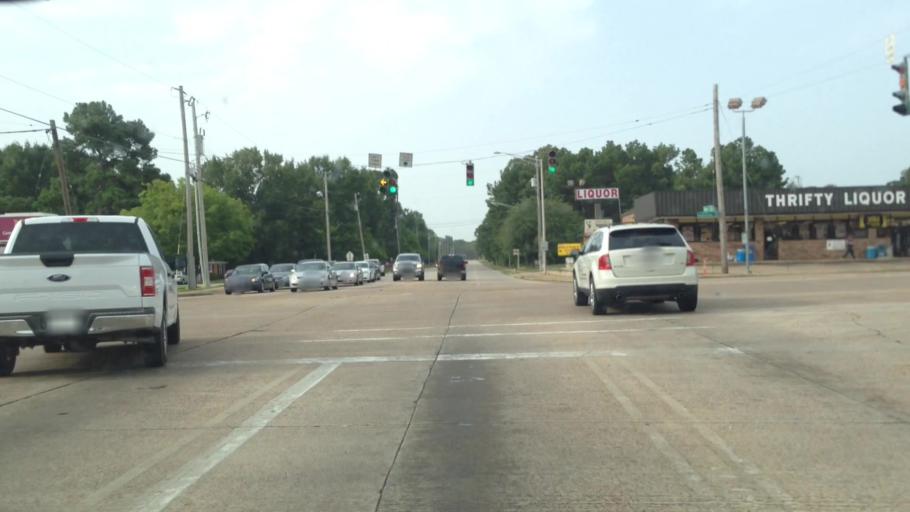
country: US
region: Louisiana
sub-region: De Soto Parish
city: Stonewall
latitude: 32.4024
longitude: -93.8147
